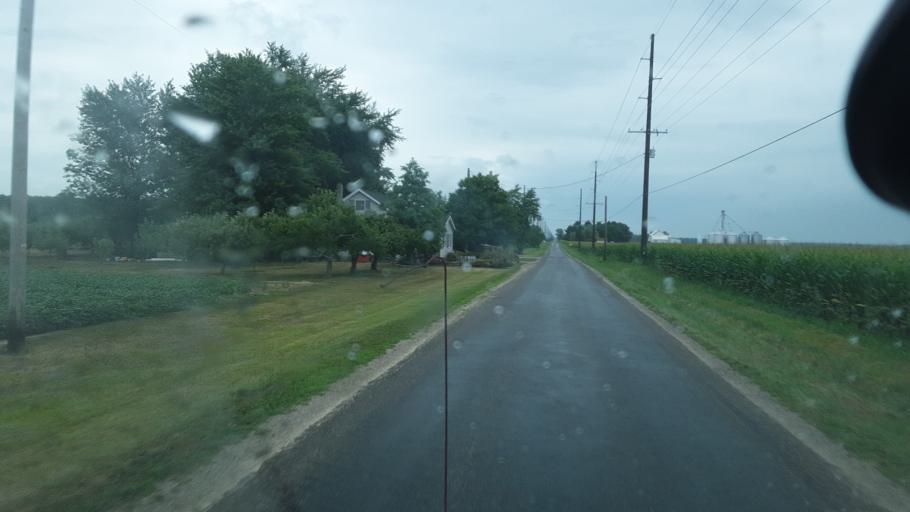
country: US
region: Ohio
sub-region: Defiance County
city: Hicksville
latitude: 41.3397
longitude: -84.6660
